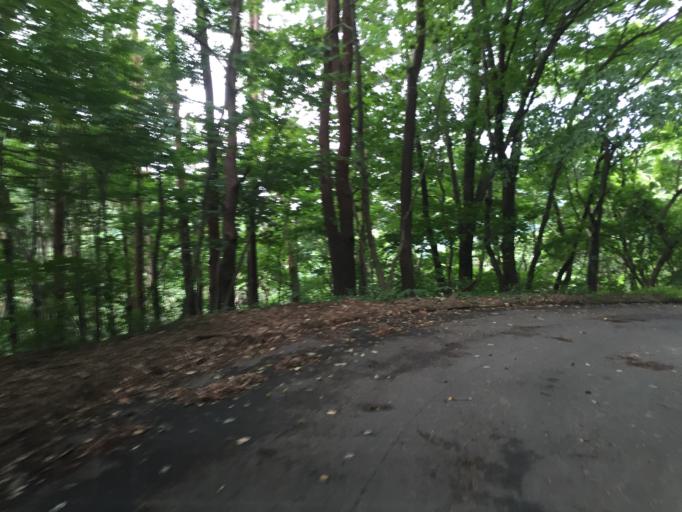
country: JP
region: Fukushima
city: Motomiya
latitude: 37.5554
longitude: 140.3023
